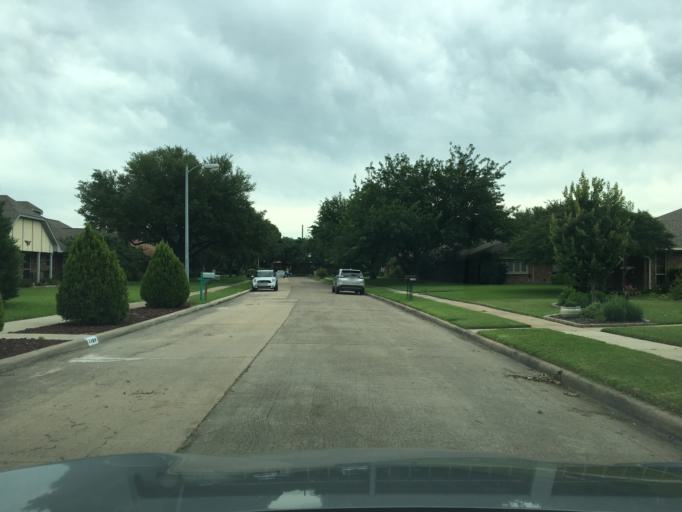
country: US
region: Texas
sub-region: Dallas County
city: Richardson
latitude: 32.9396
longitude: -96.7088
